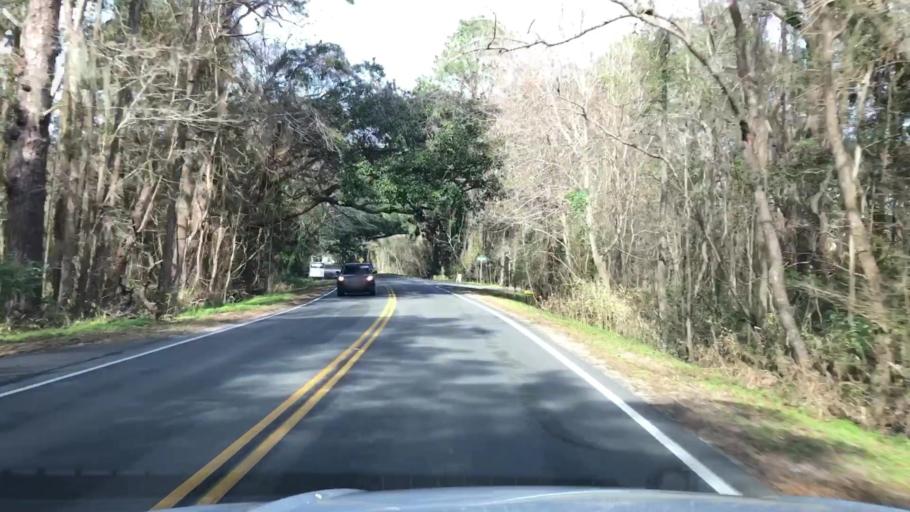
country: US
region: South Carolina
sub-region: Charleston County
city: Shell Point
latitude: 32.7258
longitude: -80.0238
